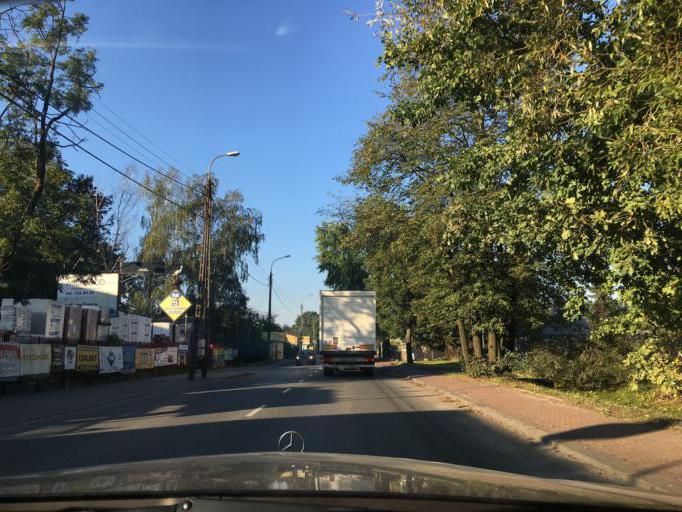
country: PL
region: Masovian Voivodeship
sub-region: Powiat grodziski
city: Milanowek
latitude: 52.1243
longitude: 20.6857
